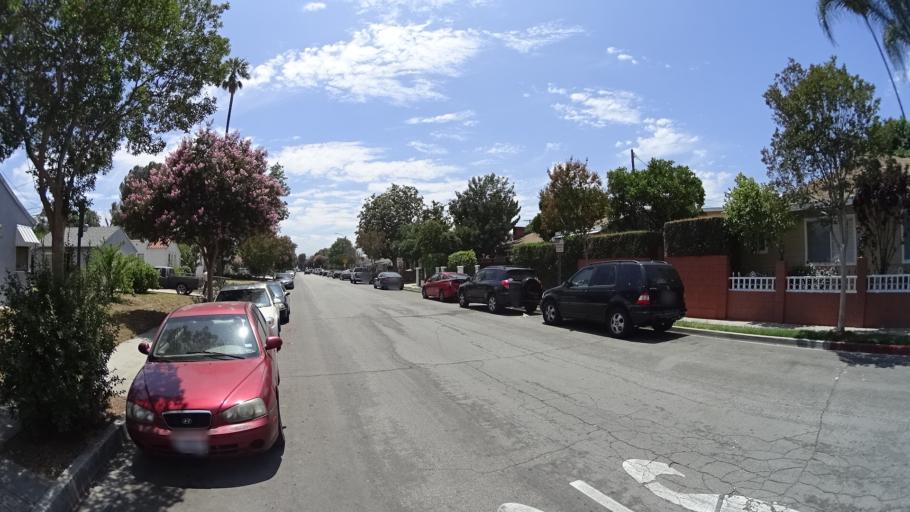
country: US
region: California
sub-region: Los Angeles County
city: Burbank
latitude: 34.1726
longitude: -118.3105
